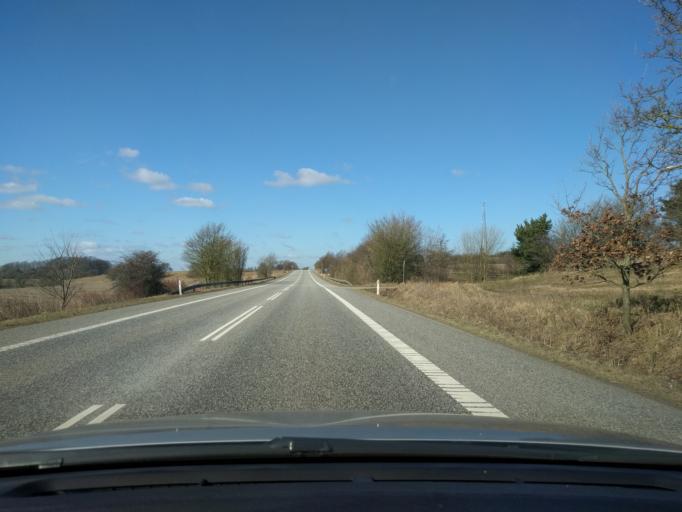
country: DK
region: South Denmark
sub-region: Aabenraa Kommune
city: Lojt Kirkeby
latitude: 55.1375
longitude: 9.4368
